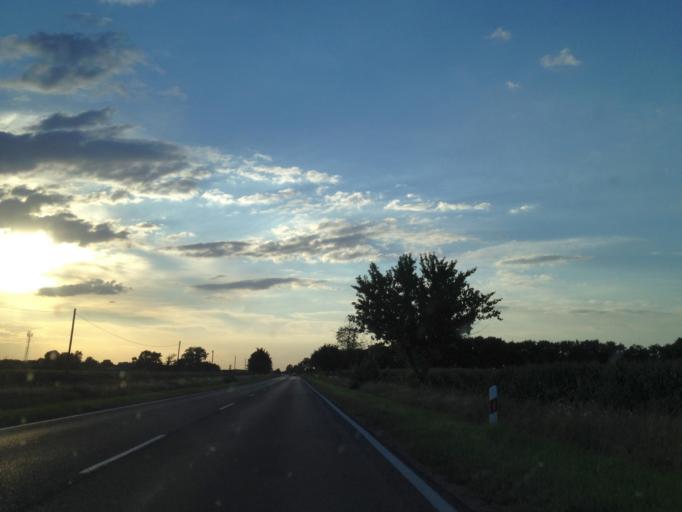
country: HU
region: Gyor-Moson-Sopron
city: Otteveny
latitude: 47.7363
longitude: 17.4746
